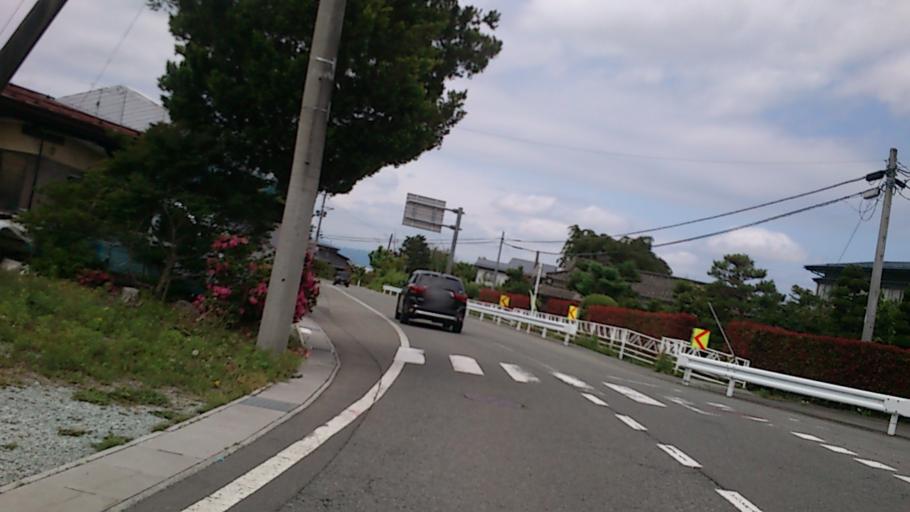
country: JP
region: Yamagata
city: Tendo
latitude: 38.3158
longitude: 140.3998
